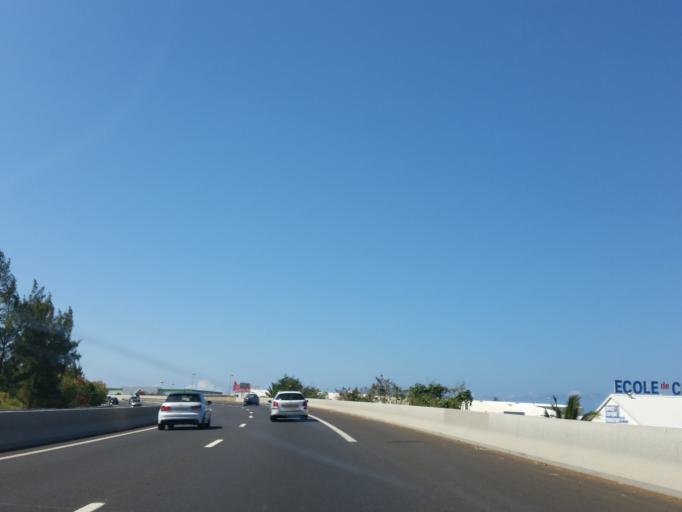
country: RE
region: Reunion
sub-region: Reunion
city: Saint-Louis
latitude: -21.2904
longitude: 55.4017
